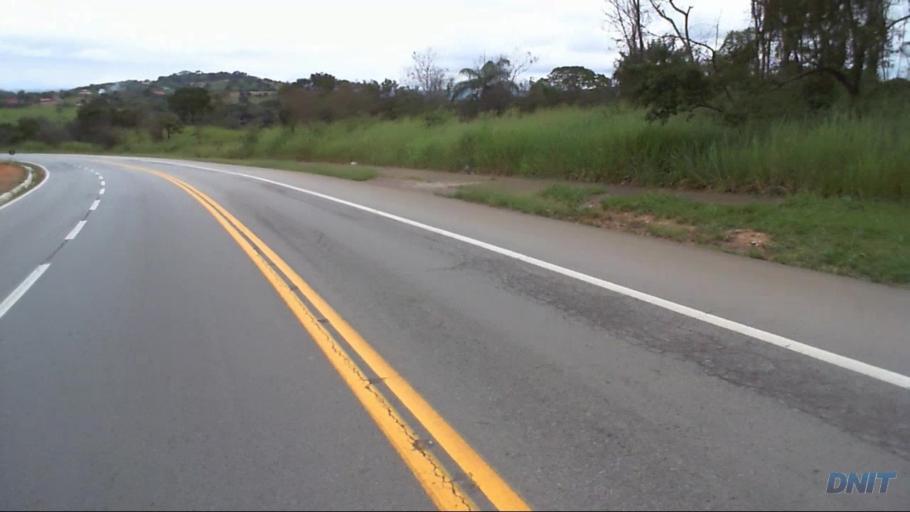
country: BR
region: Minas Gerais
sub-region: Barao De Cocais
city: Barao de Cocais
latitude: -19.7577
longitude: -43.4711
